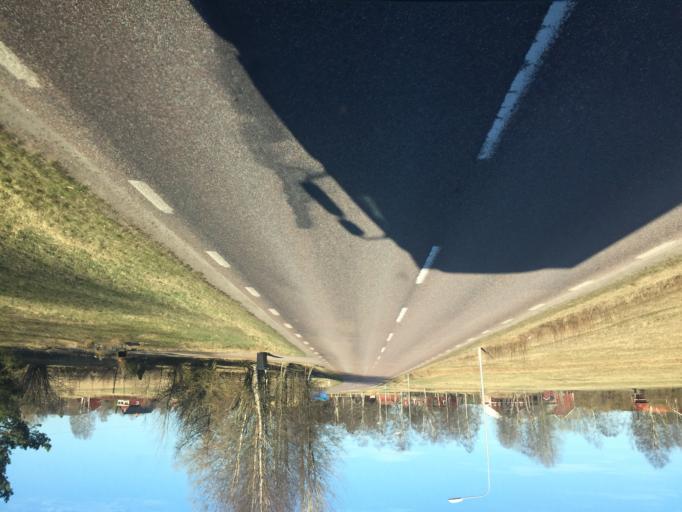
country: SE
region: Dalarna
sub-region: Vansbro Kommun
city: Jarna
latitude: 60.4527
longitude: 14.5010
